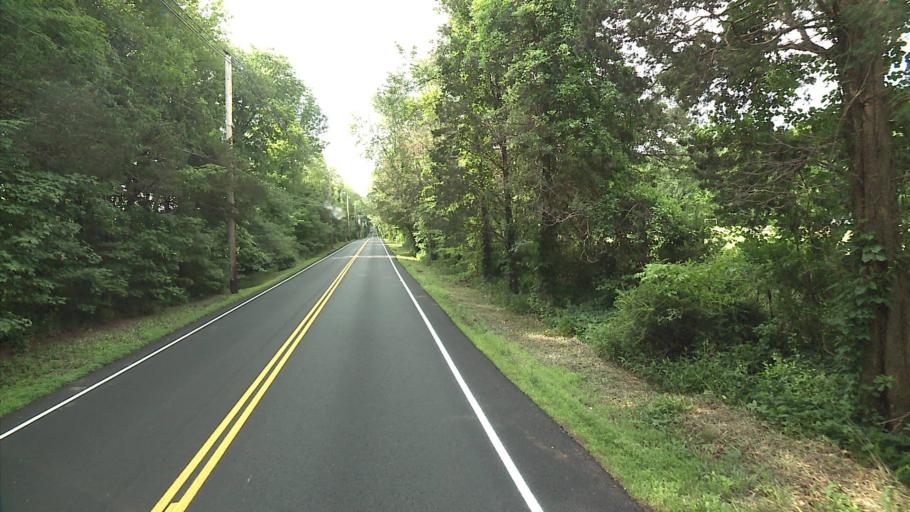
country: US
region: Connecticut
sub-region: New Haven County
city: Wallingford Center
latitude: 41.4145
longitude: -72.8000
